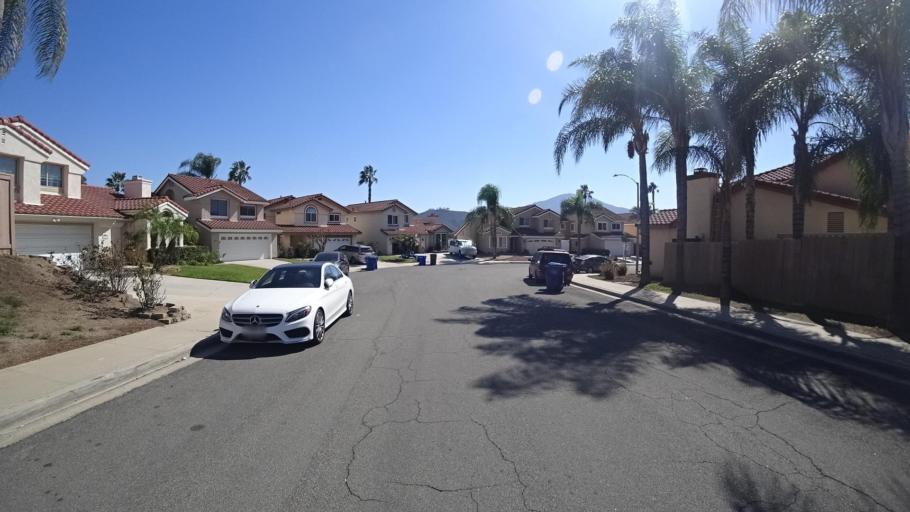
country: US
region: California
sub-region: San Diego County
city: Rancho San Diego
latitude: 32.7489
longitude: -116.9358
